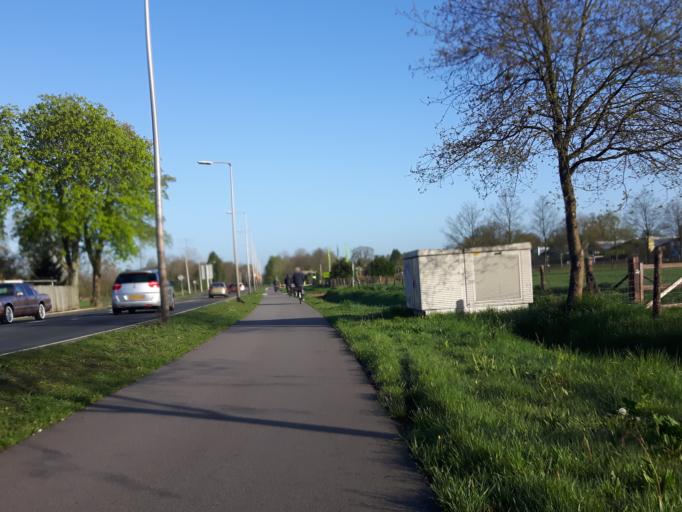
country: NL
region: Overijssel
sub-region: Gemeente Enschede
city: Enschede
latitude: 52.2058
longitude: 6.8539
